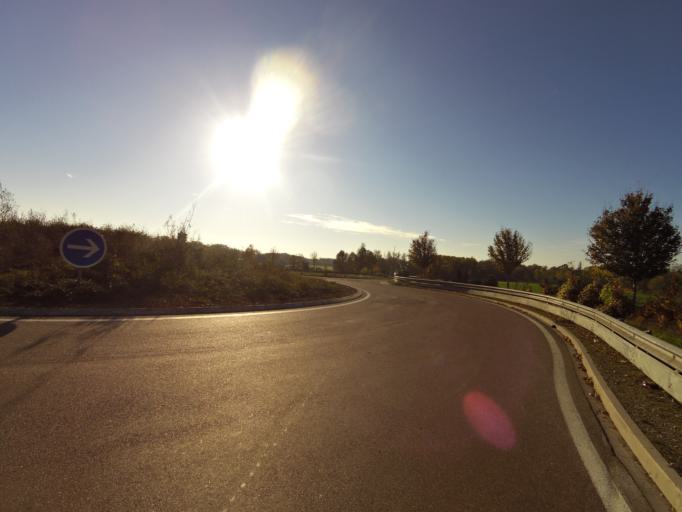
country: FR
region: Champagne-Ardenne
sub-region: Departement de l'Aube
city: Bucheres
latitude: 48.2508
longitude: 4.1120
